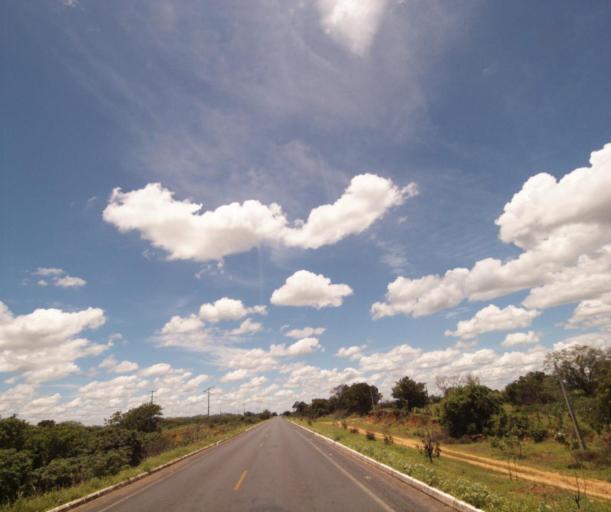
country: BR
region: Bahia
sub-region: Bom Jesus Da Lapa
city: Bom Jesus da Lapa
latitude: -13.2578
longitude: -43.4676
